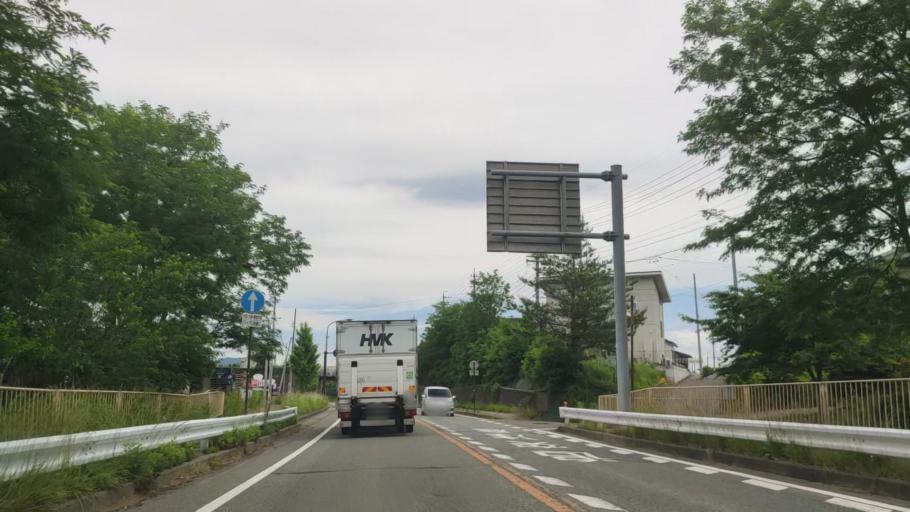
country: JP
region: Nagano
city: Komoro
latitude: 36.3152
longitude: 138.4457
